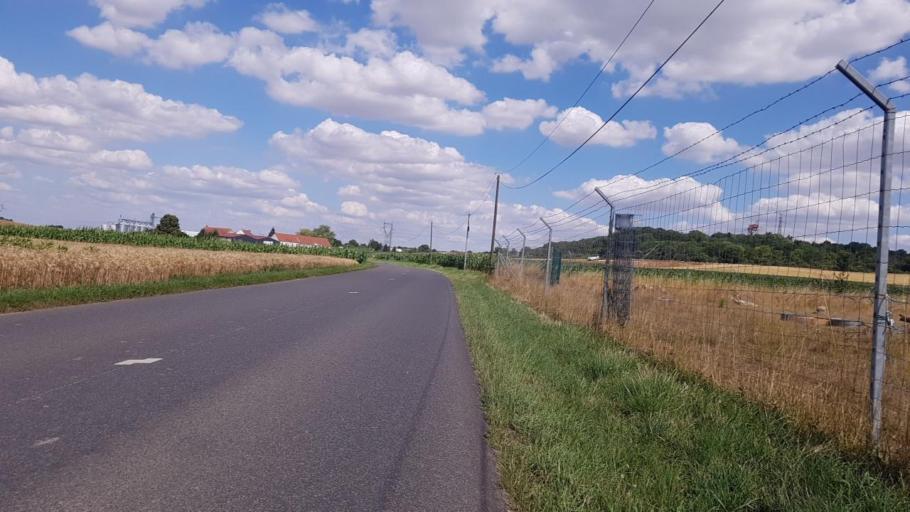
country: FR
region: Ile-de-France
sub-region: Departement de Seine-et-Marne
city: Moussy-le-Vieux
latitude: 49.0696
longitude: 2.6328
